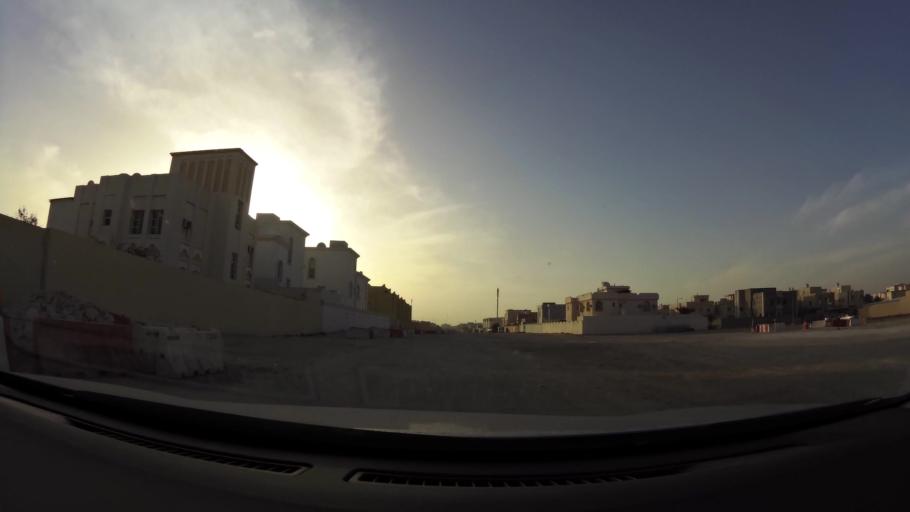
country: QA
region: Al Wakrah
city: Al Wakrah
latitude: 25.1474
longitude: 51.6105
